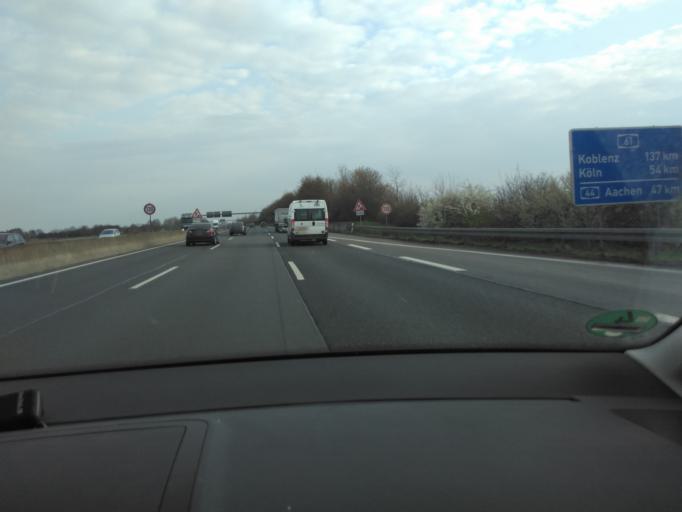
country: DE
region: North Rhine-Westphalia
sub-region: Regierungsbezirk Dusseldorf
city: Juchen
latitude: 51.0878
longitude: 6.4210
